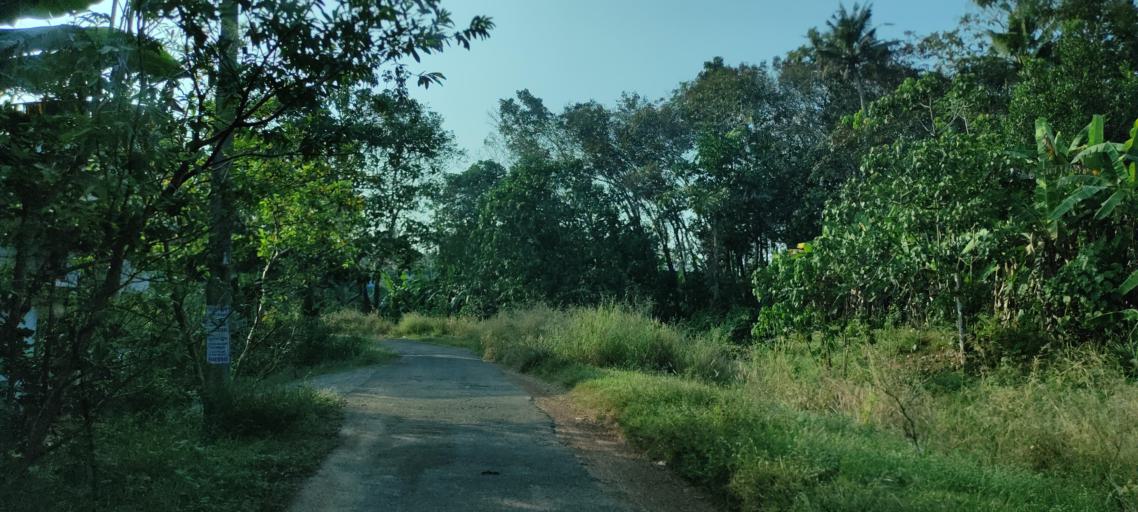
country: IN
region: Kerala
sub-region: Pattanamtitta
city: Adur
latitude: 9.1360
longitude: 76.7302
